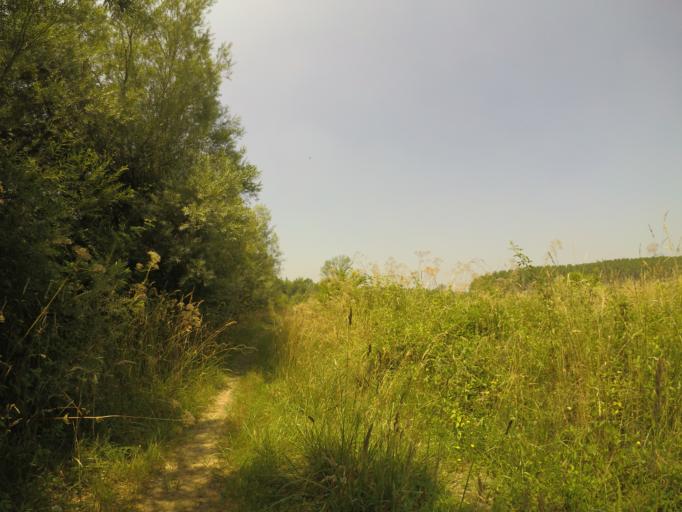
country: IT
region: Friuli Venezia Giulia
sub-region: Provincia di Udine
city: Bertiolo
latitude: 45.9157
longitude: 13.0576
